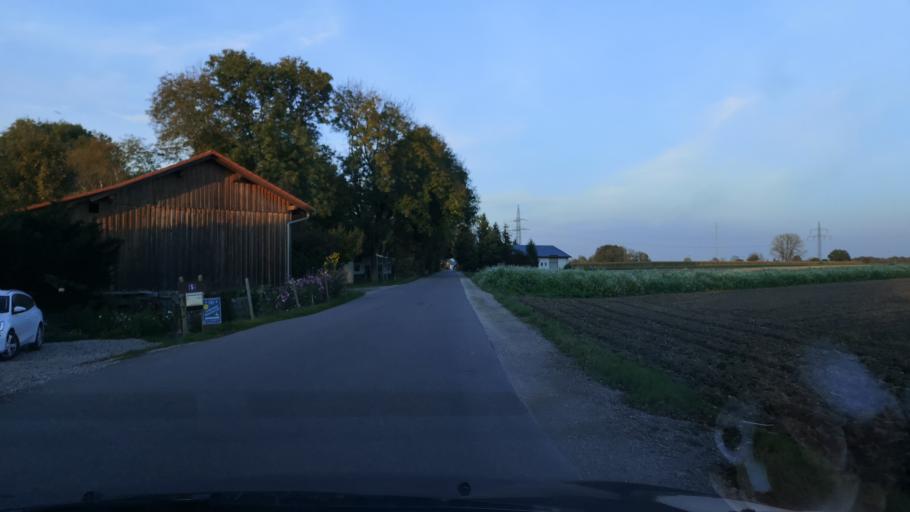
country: DE
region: Bavaria
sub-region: Upper Bavaria
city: Ismaning
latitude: 48.2325
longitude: 11.7134
